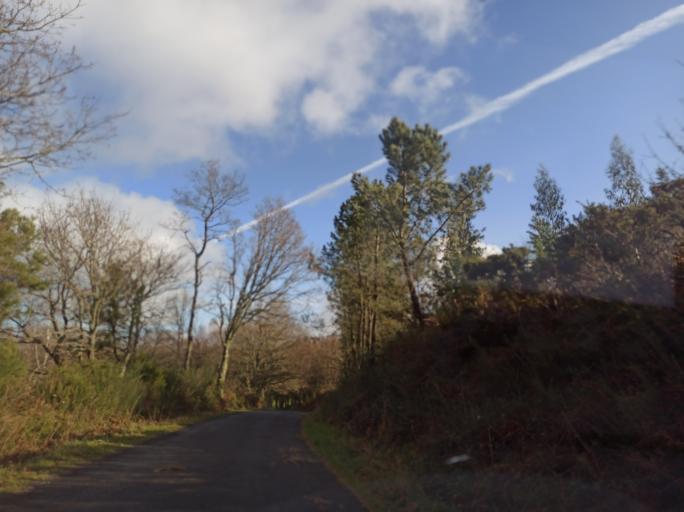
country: ES
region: Galicia
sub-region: Provincia da Coruna
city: Sobrado
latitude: 43.0805
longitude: -7.9510
